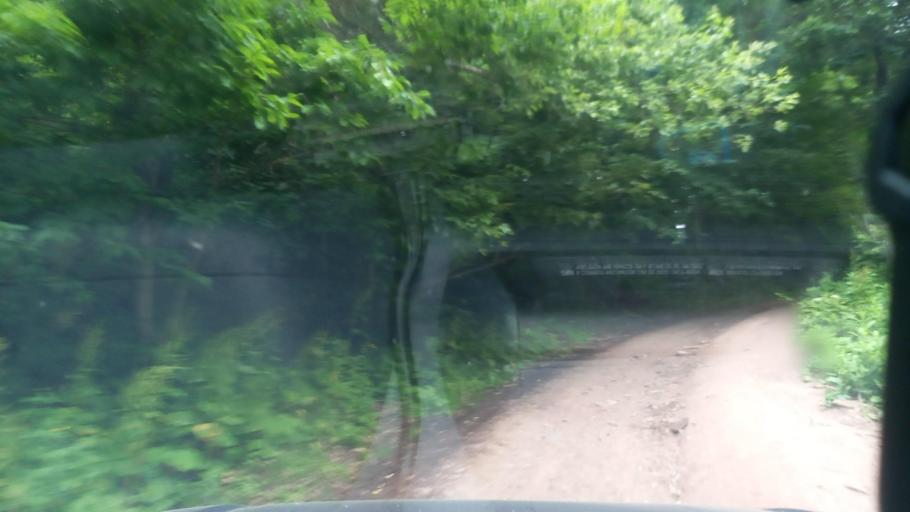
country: RU
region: Karachayevo-Cherkesiya
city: Kurdzhinovo
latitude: 43.8077
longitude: 40.8551
